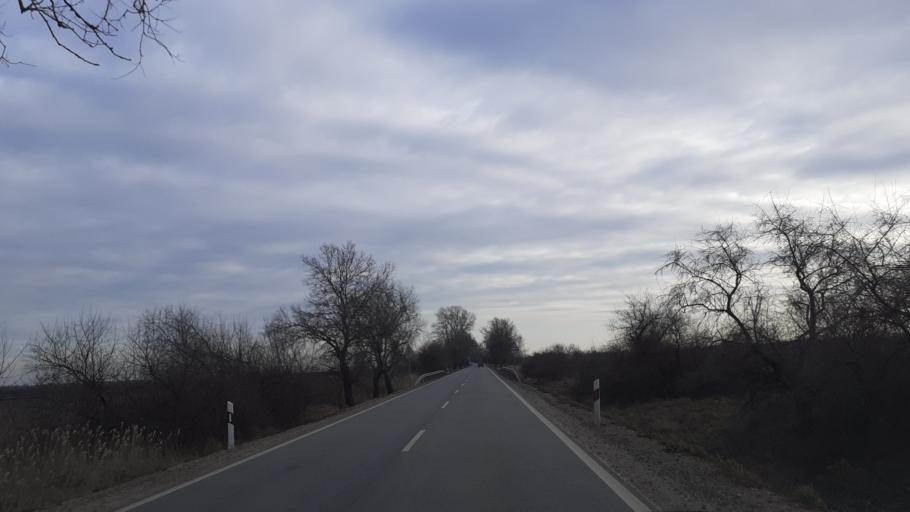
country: HU
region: Fejer
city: Sarkeresztur
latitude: 46.9840
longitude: 18.5656
